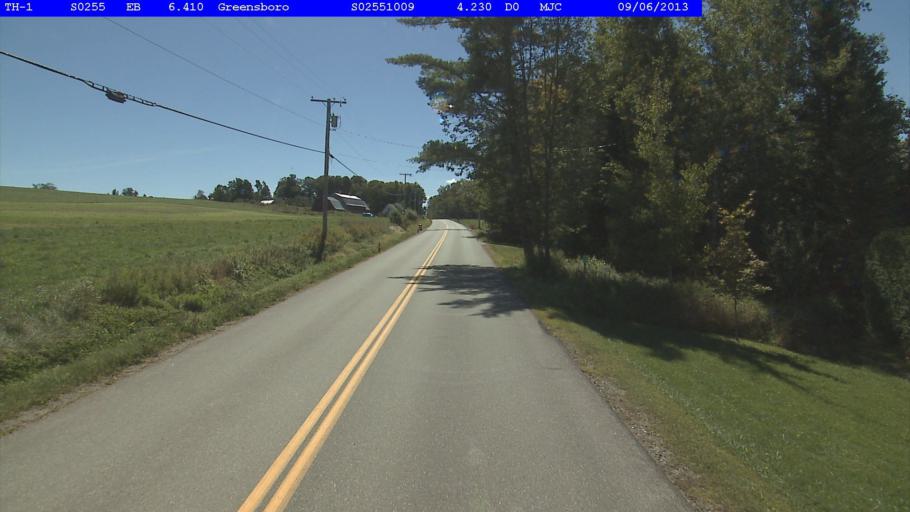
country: US
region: Vermont
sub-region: Caledonia County
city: Hardwick
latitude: 44.5878
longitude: -72.2985
